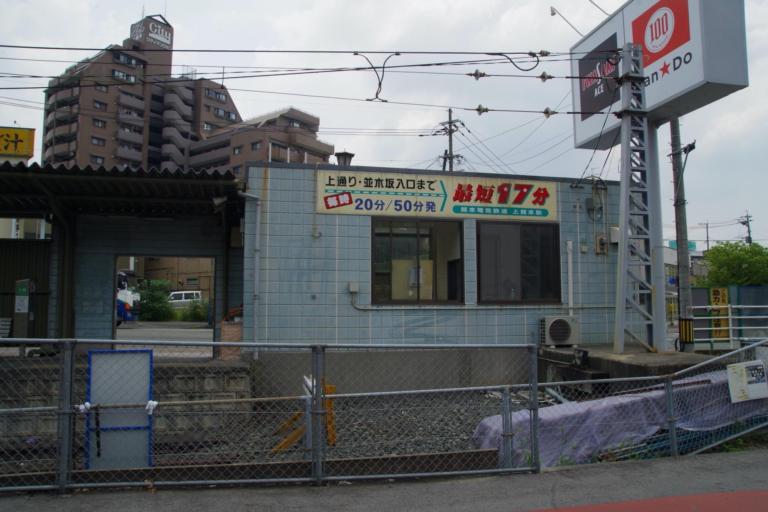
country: JP
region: Kumamoto
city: Kumamoto
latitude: 32.8184
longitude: 130.6998
